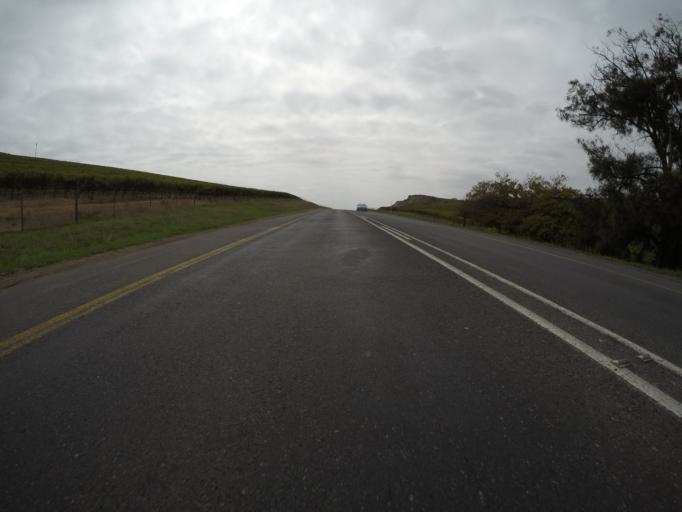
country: ZA
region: Western Cape
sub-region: City of Cape Town
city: Sunset Beach
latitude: -33.8346
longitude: 18.5908
